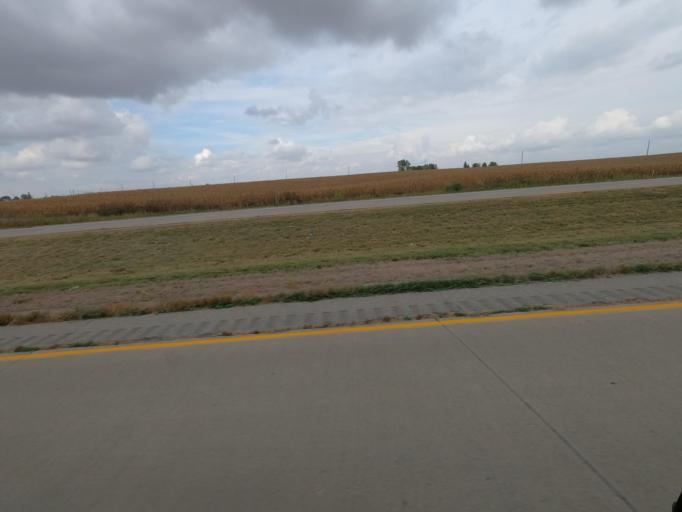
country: US
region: Iowa
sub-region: Jasper County
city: Prairie City
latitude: 41.5880
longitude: -93.2059
